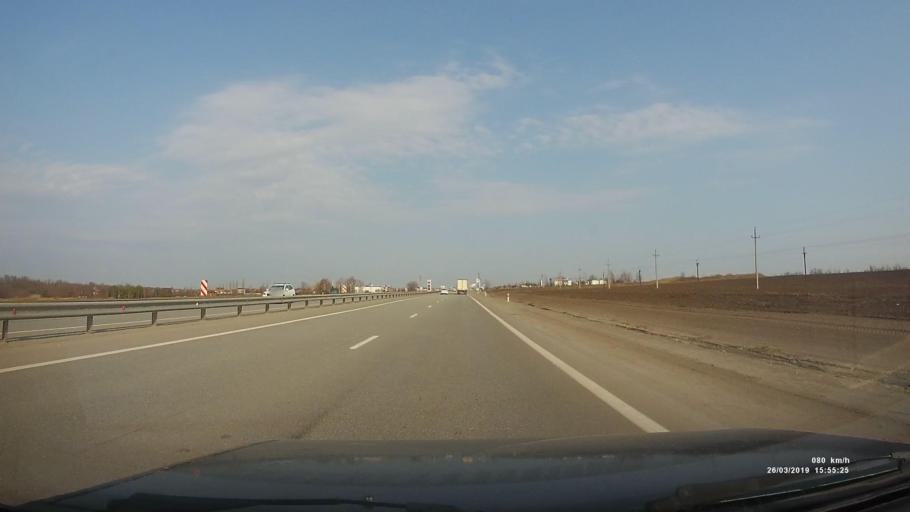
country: RU
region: Rostov
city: Kalinin
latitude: 47.2666
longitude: 39.5752
